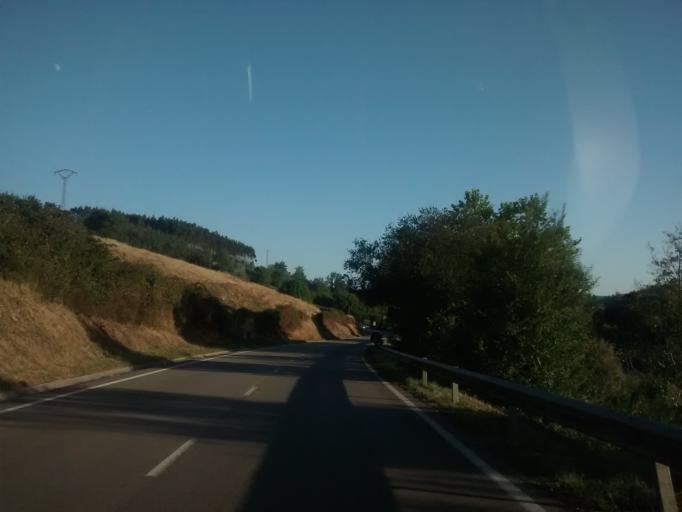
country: ES
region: Cantabria
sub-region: Provincia de Cantabria
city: San Miguel de Meruelo
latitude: 43.4679
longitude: -3.5861
